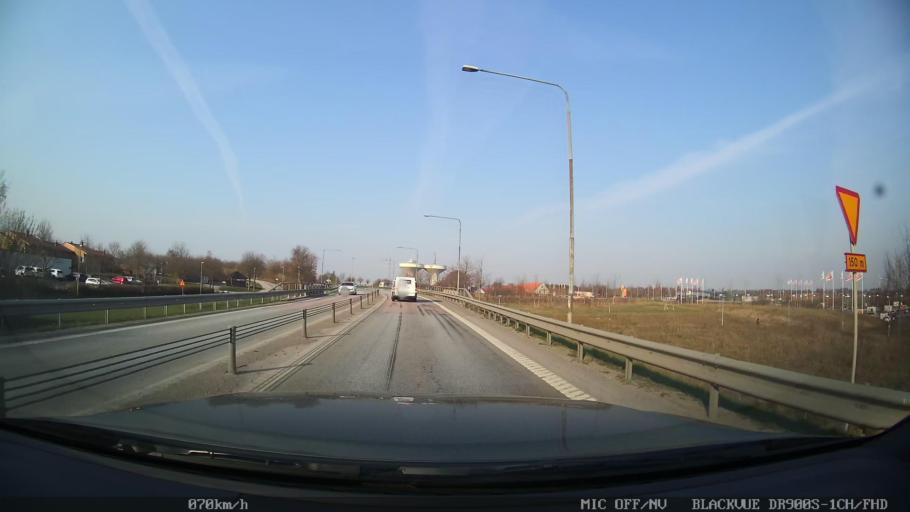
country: SE
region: Skane
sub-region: Ystads Kommun
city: Ystad
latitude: 55.4437
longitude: 13.8099
